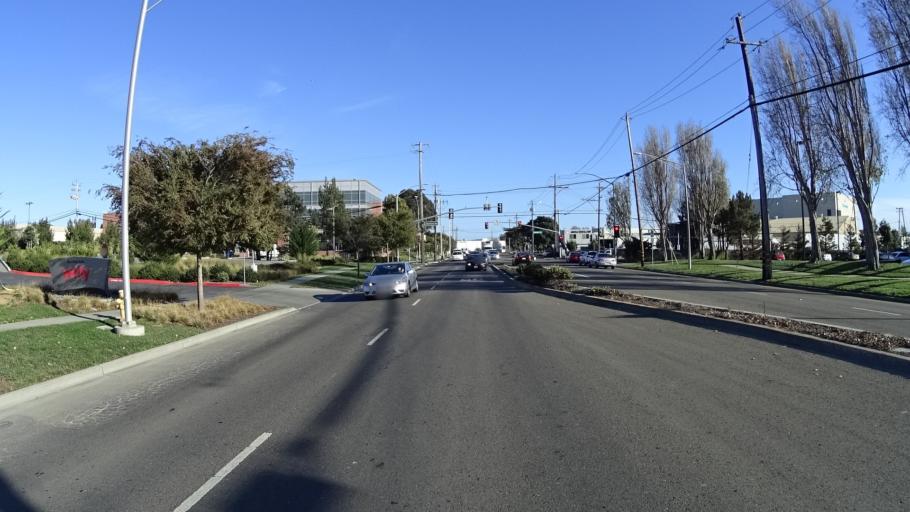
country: US
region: California
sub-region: San Mateo County
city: South San Francisco
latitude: 37.6531
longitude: -122.3947
